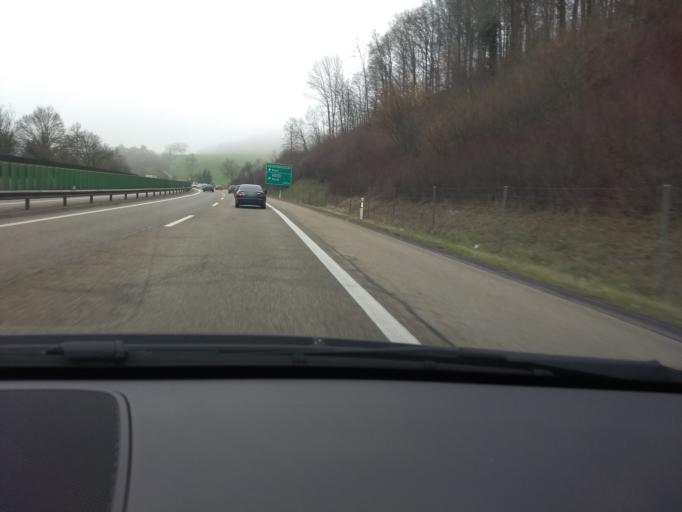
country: CH
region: Basel-Landschaft
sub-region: Bezirk Liestal
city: Arisdorf
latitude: 47.5229
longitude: 7.7515
